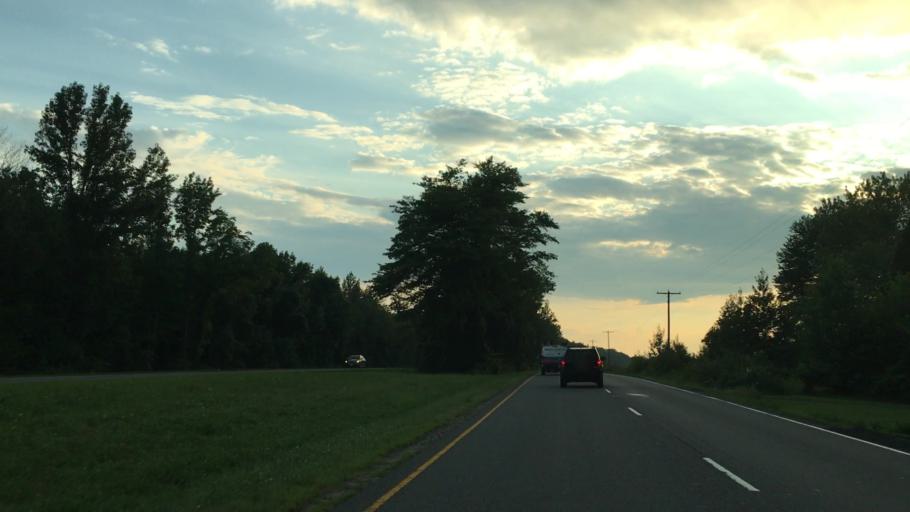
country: US
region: Virginia
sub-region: Spotsylvania County
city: Spotsylvania
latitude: 38.3106
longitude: -77.6621
